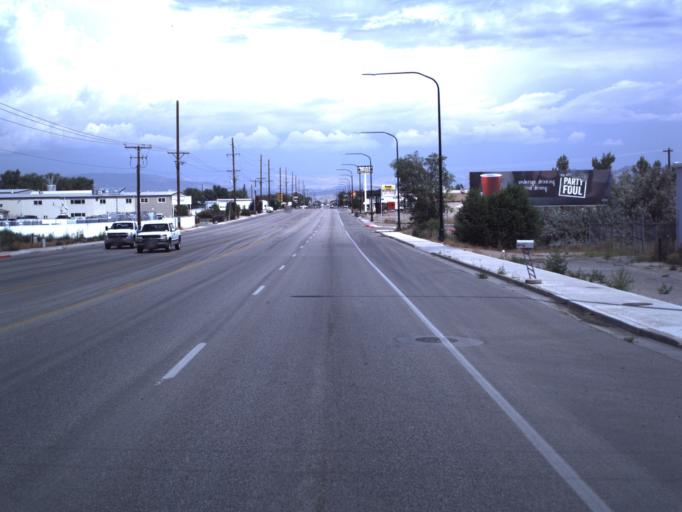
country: US
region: Utah
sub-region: Uintah County
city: Naples
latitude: 40.4304
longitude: -109.4994
